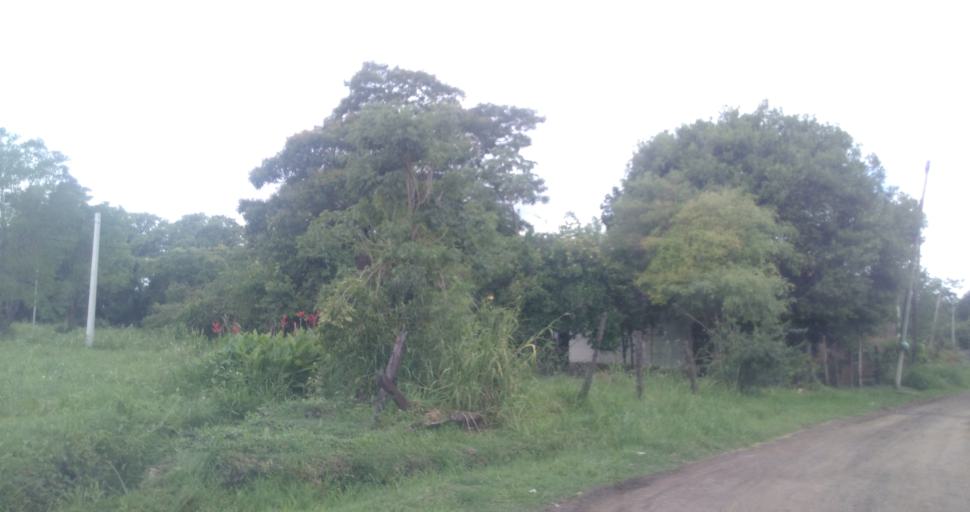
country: AR
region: Chaco
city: Fontana
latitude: -27.4191
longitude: -59.0345
